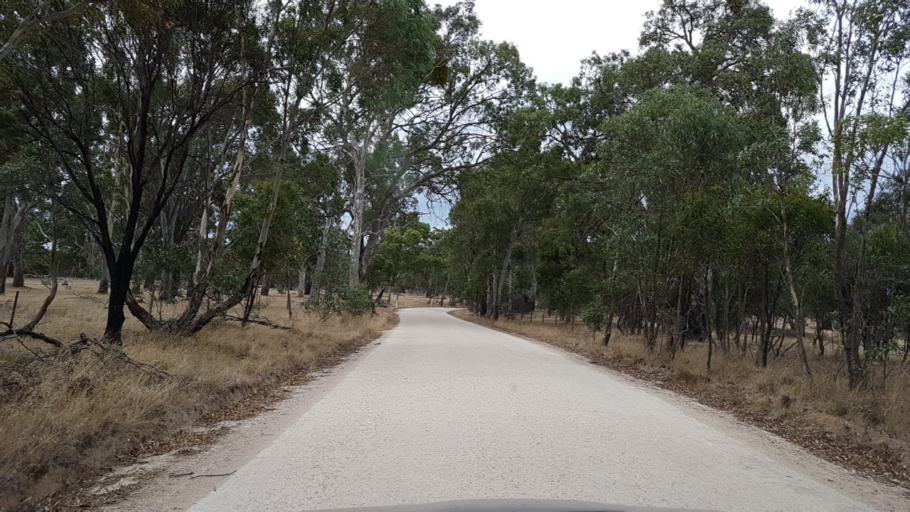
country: AU
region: South Australia
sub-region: Adelaide Hills
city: Birdwood
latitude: -34.7879
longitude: 138.9741
